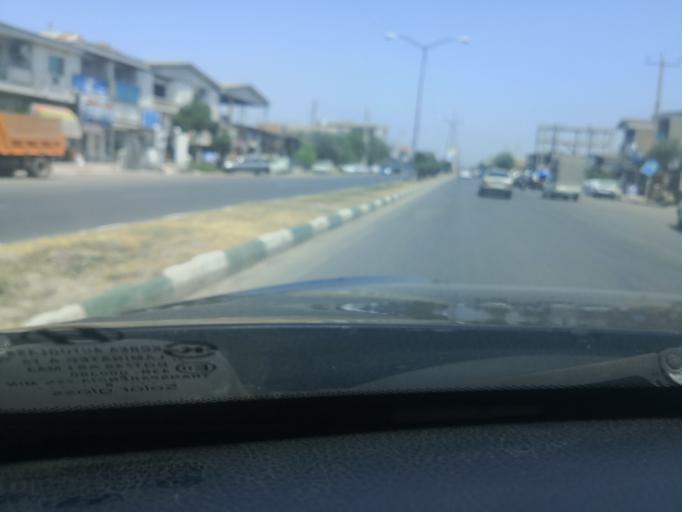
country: IR
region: Golestan
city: Aq Qala
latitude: 37.0093
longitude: 54.4625
